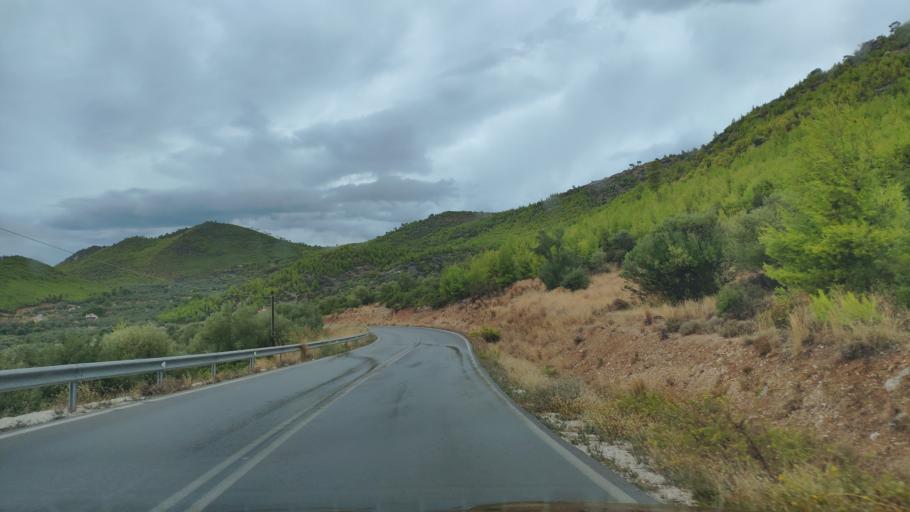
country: GR
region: Peloponnese
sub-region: Nomos Korinthias
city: Perachora
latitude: 38.0324
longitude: 22.9263
